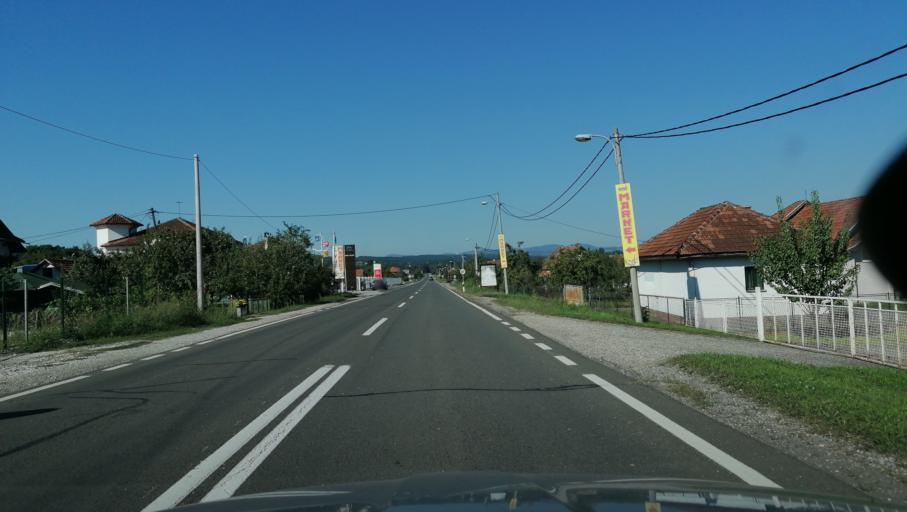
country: RS
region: Central Serbia
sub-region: Raski Okrug
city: Kraljevo
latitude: 43.6832
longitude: 20.5742
